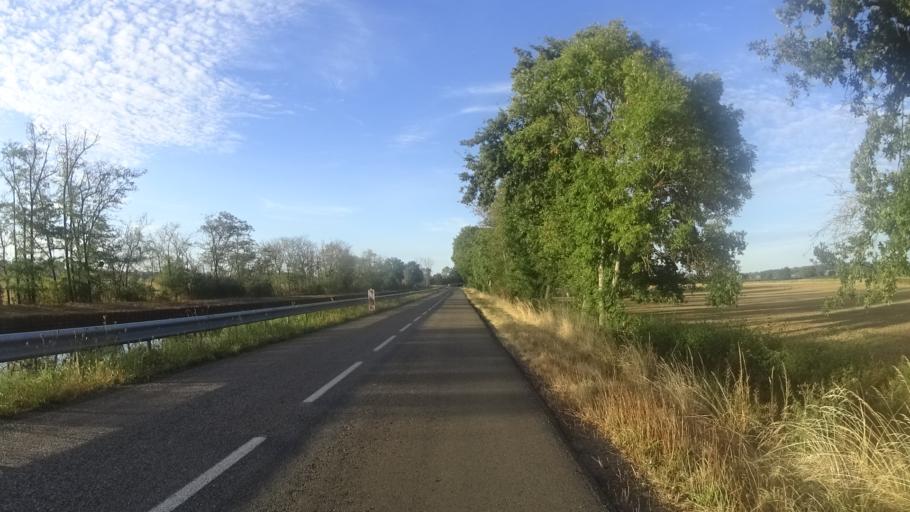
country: FR
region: Bourgogne
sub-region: Departement de Saone-et-Loire
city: Palinges
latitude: 46.5206
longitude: 4.1960
